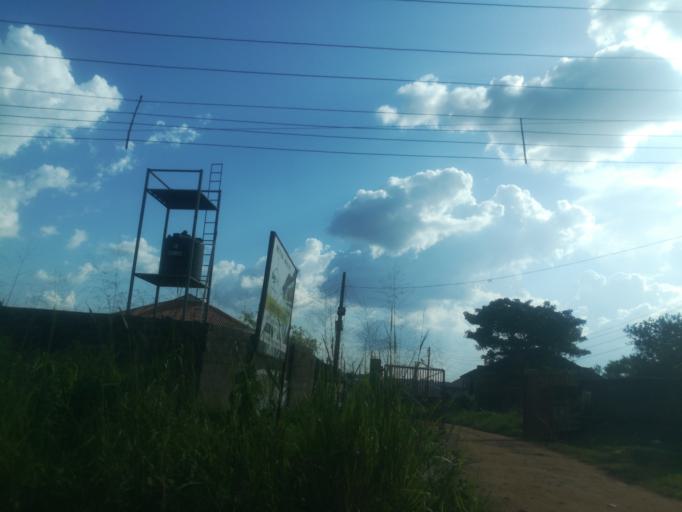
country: NG
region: Oyo
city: Ibadan
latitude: 7.4351
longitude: 3.9742
